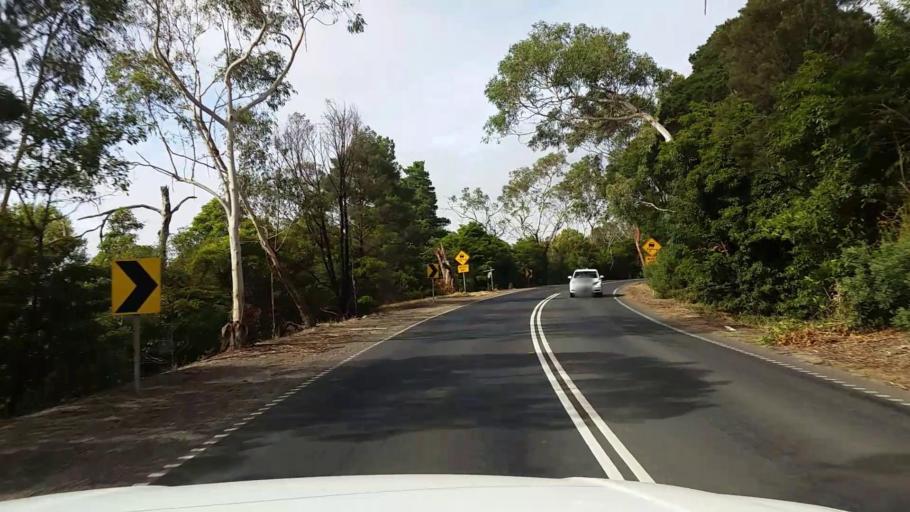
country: AU
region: Victoria
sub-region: Mornington Peninsula
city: Mount Martha
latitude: -38.2890
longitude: 145.0748
